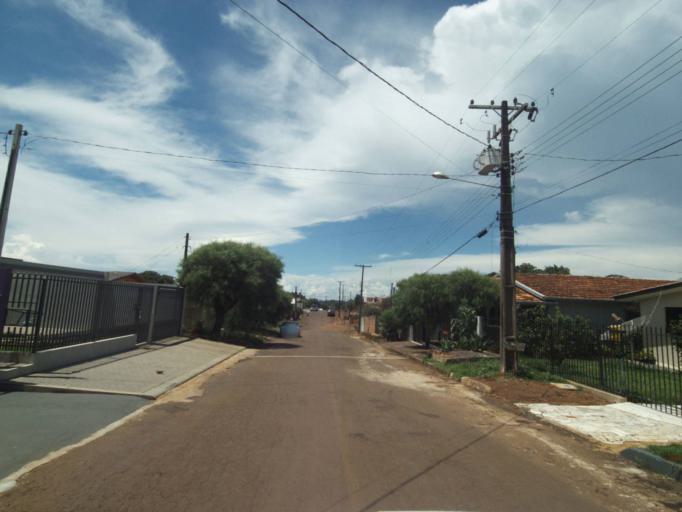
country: BR
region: Parana
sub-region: Guaraniacu
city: Guaraniacu
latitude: -25.0954
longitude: -52.8766
